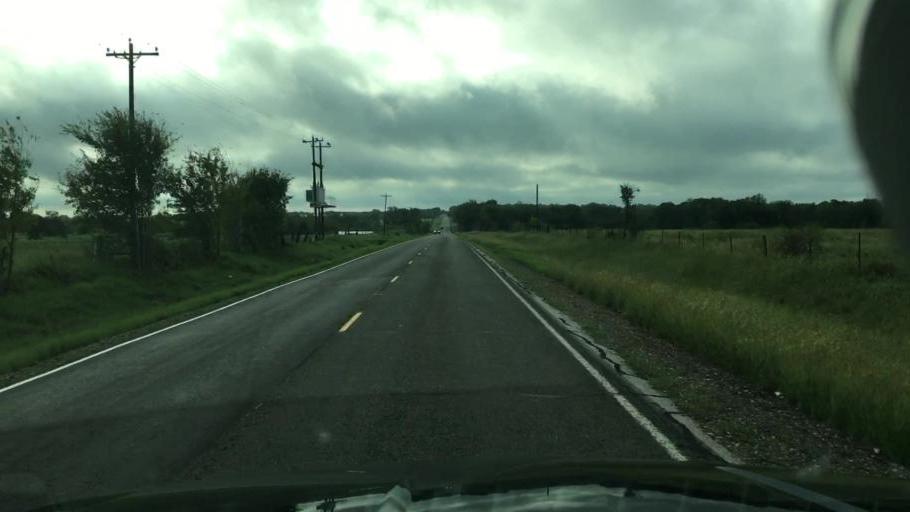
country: US
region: Texas
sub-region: Lee County
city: Lexington
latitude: 30.3732
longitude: -96.8447
